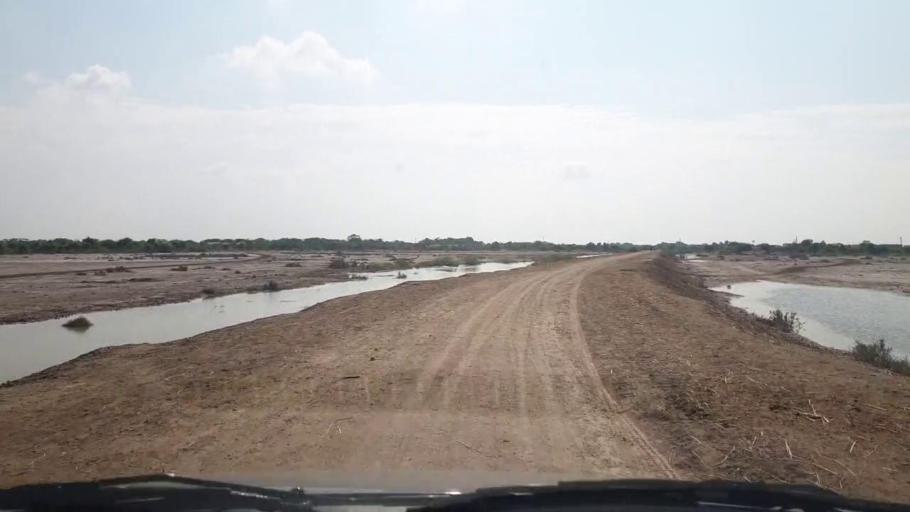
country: PK
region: Sindh
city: Badin
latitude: 24.4830
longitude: 68.6123
